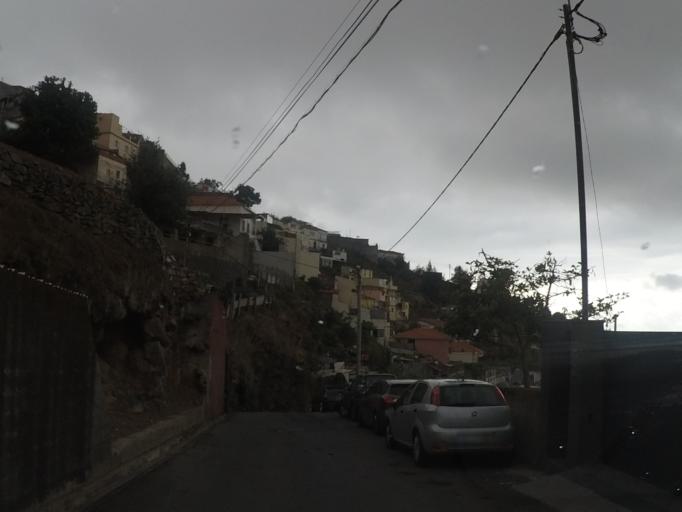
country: PT
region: Madeira
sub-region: Funchal
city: Nossa Senhora do Monte
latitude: 32.6734
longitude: -16.9138
